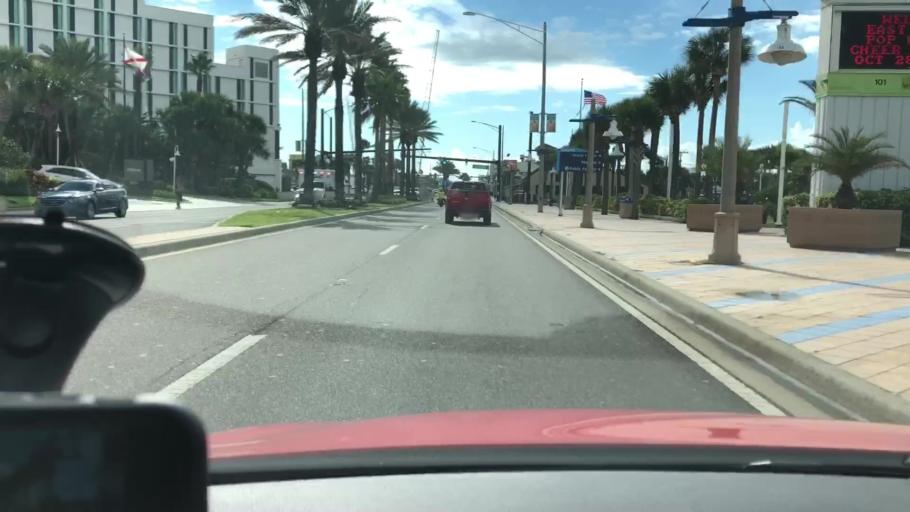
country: US
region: Florida
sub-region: Volusia County
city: Daytona Beach
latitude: 29.2292
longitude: -81.0095
